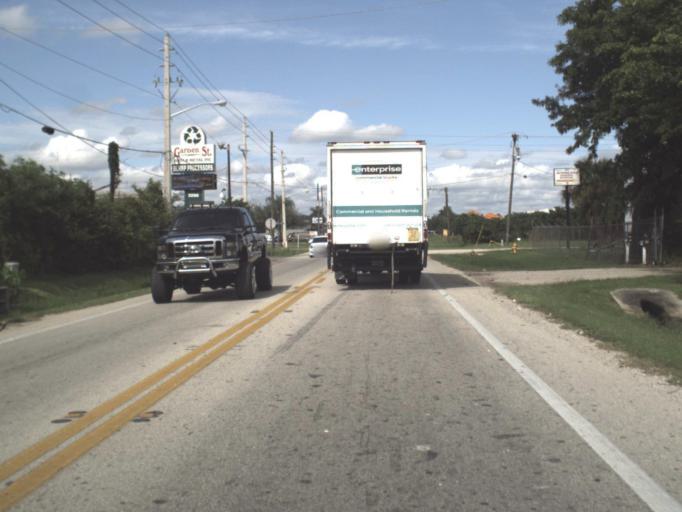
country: US
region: Florida
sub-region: Lee County
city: Fort Myers
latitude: 26.6183
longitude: -81.8519
